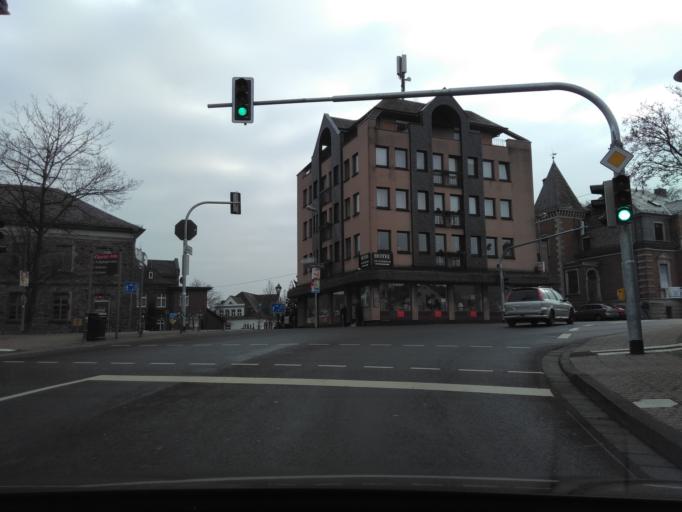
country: DE
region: Rheinland-Pfalz
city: Montabaur
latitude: 50.4343
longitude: 7.8320
